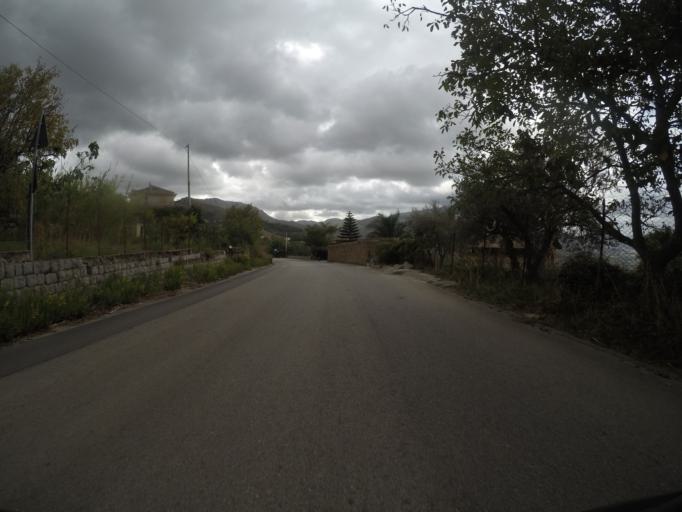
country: IT
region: Sicily
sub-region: Palermo
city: Montelepre
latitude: 38.0947
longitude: 13.1720
